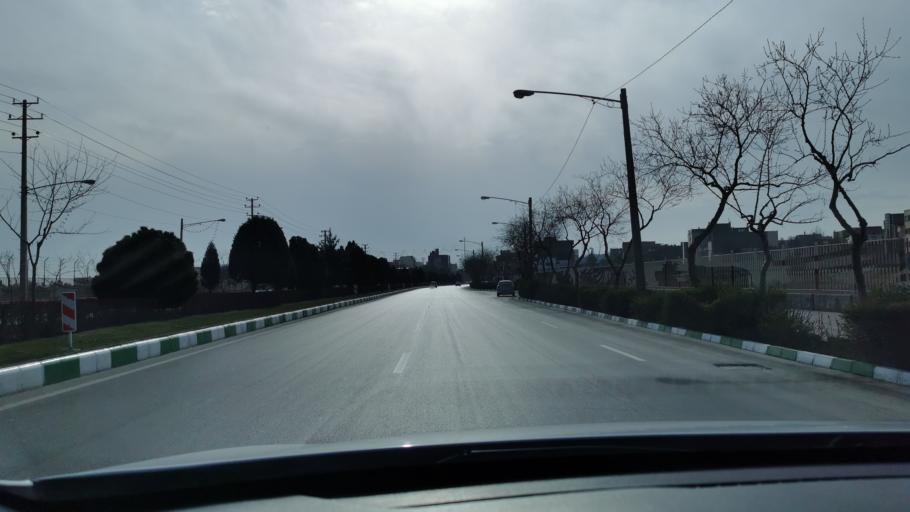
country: IR
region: Razavi Khorasan
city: Mashhad
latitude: 36.3005
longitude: 59.5210
